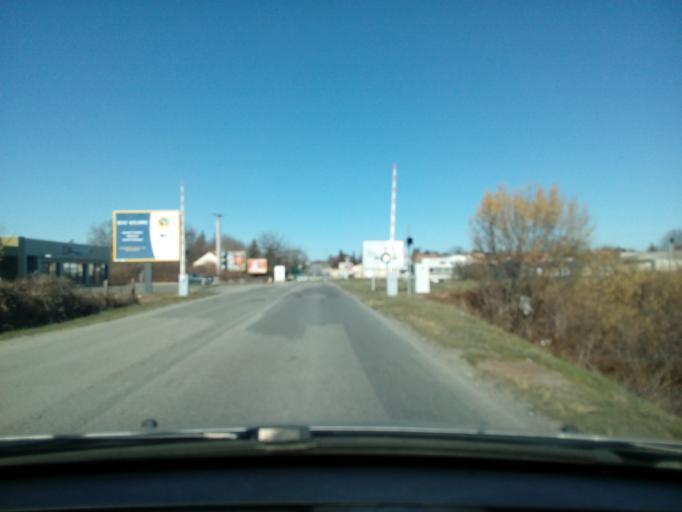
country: FR
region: Limousin
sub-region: Departement de la Creuse
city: Gueret
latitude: 46.1907
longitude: 1.8753
